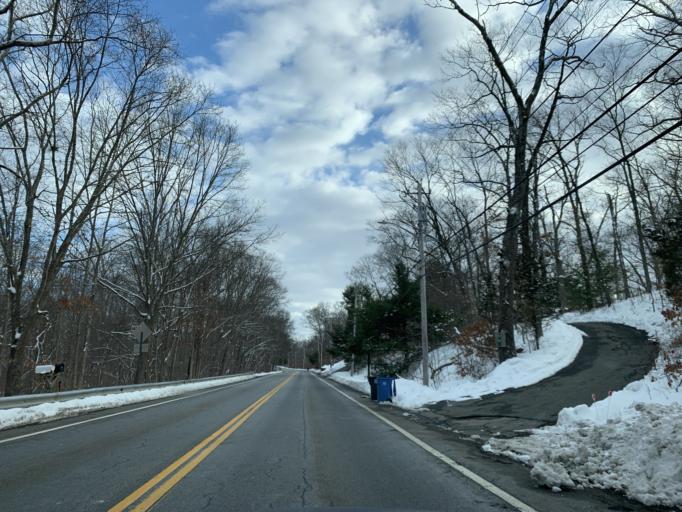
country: US
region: Rhode Island
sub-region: Providence County
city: Cumberland Hill
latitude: 41.9866
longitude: -71.4609
